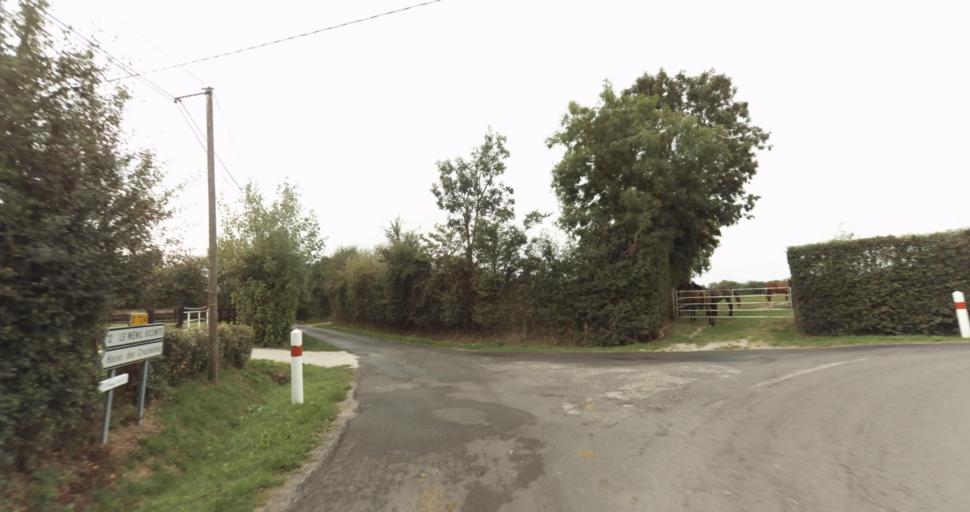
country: FR
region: Lower Normandy
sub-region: Departement de l'Orne
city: Gace
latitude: 48.7341
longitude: 0.2948
